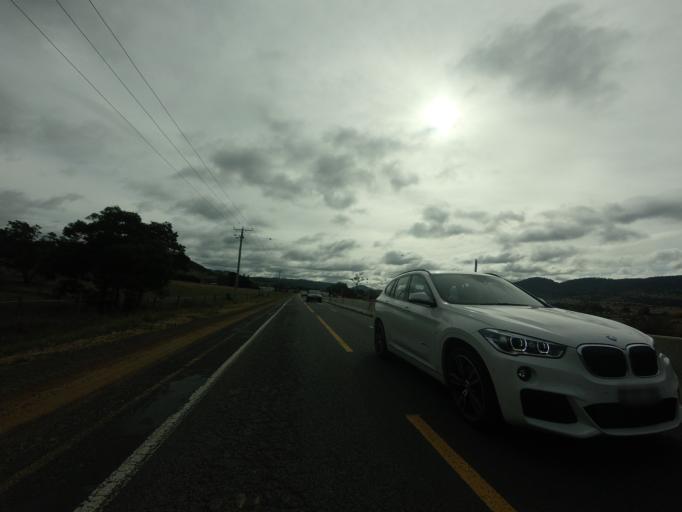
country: AU
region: Tasmania
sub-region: Brighton
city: Bridgewater
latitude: -42.6616
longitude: 147.2476
